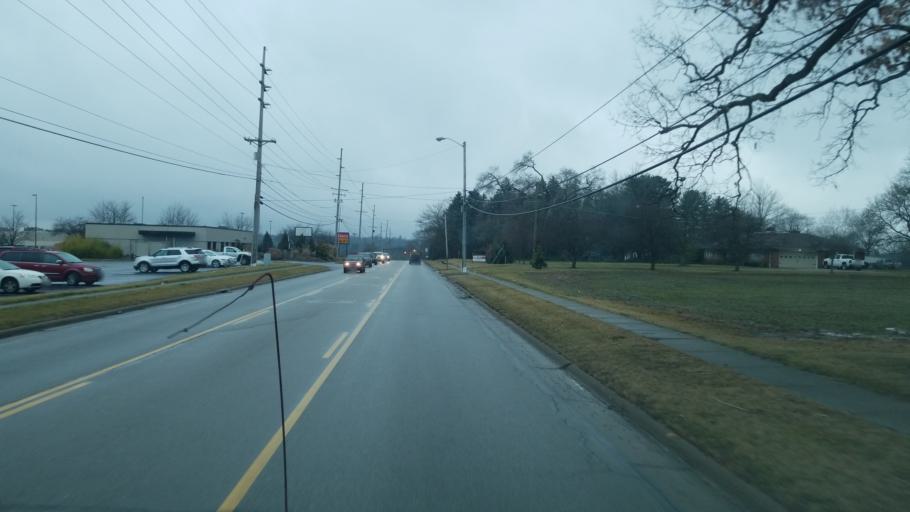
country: US
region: Ohio
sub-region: Wayne County
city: Wooster
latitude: 40.8284
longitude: -81.9107
